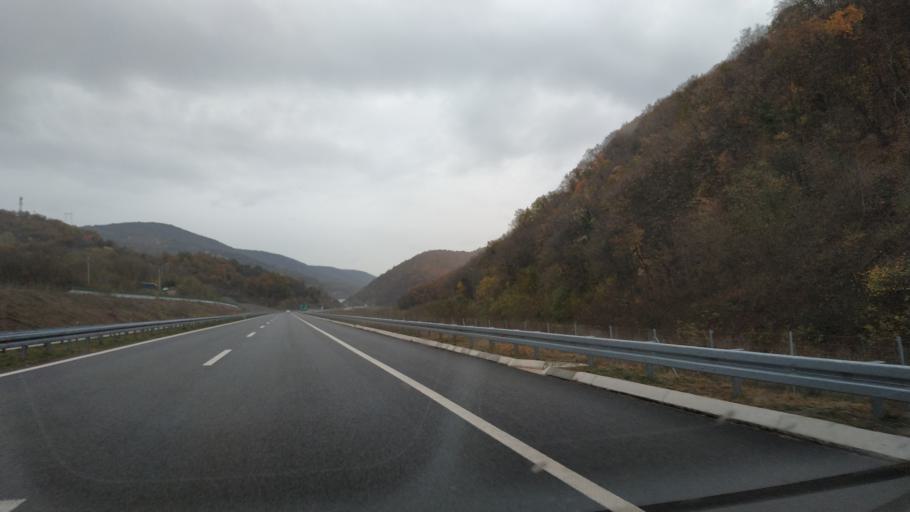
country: RS
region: Central Serbia
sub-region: Nisavski Okrug
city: Niska Banja
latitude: 43.2981
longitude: 22.0713
